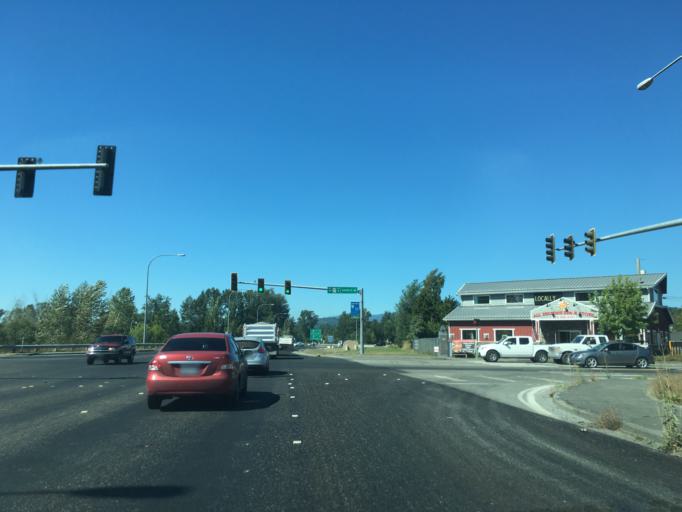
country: US
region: Washington
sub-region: Snohomish County
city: Arlington
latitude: 48.1985
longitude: -122.1294
